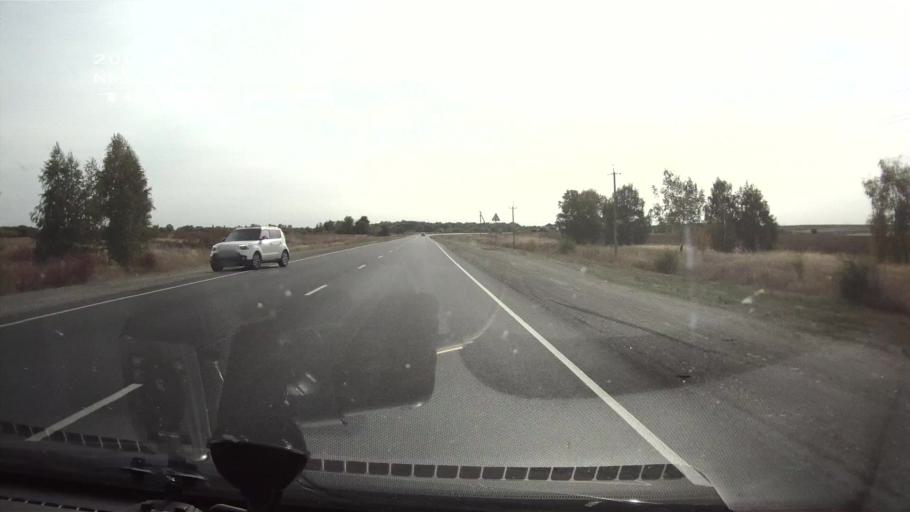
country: RU
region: Saratov
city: Sinodskoye
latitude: 52.0551
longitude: 46.7574
